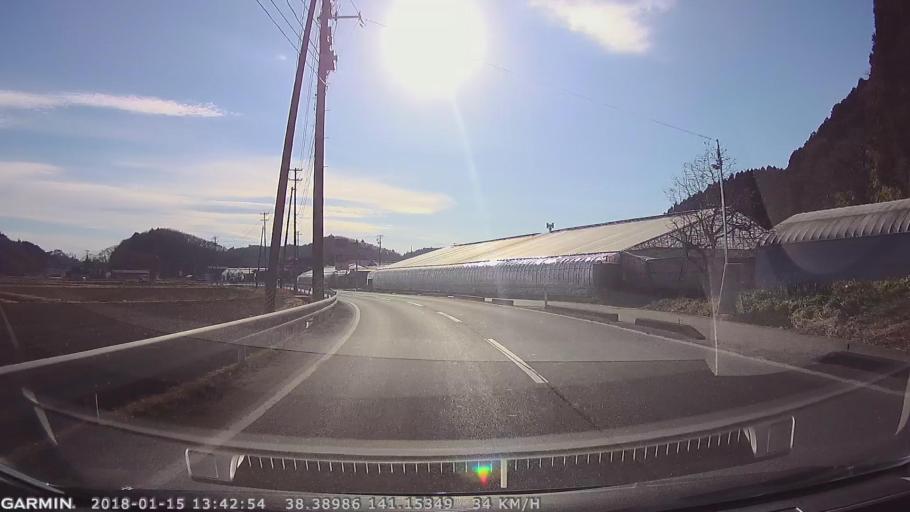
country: JP
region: Miyagi
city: Yamoto
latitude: 38.3894
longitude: 141.1531
